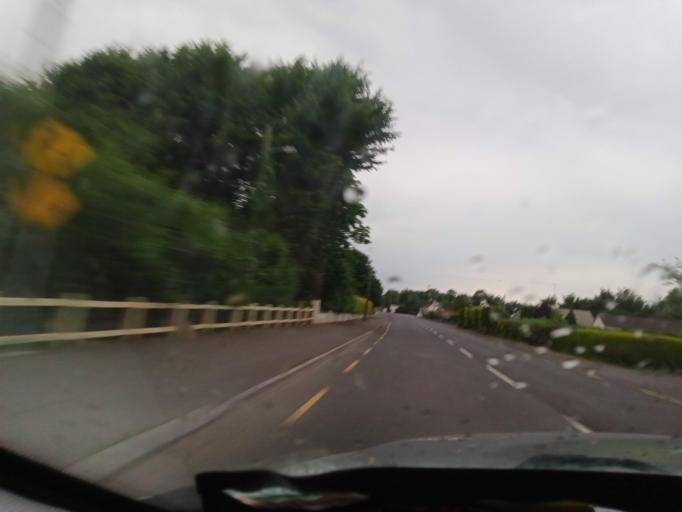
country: IE
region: Leinster
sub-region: Uibh Fhaili
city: Tullamore
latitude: 53.1471
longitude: -7.5143
